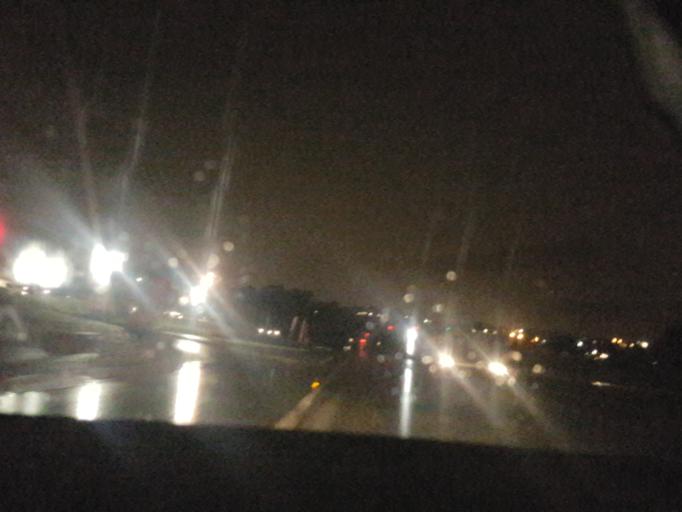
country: ZA
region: Gauteng
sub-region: City of Johannesburg Metropolitan Municipality
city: Diepsloot
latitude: -25.9572
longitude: 27.9157
